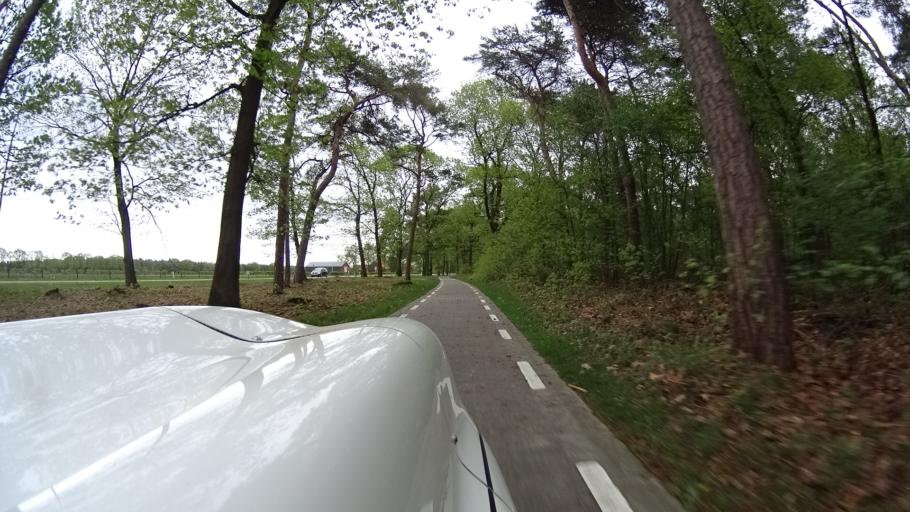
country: NL
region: North Brabant
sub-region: Gemeente Boxmeer
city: Overloon
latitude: 51.5403
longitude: 5.8741
